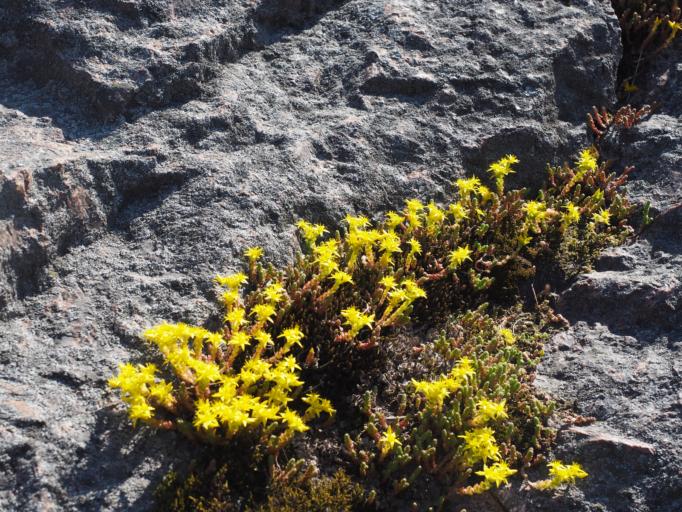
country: RU
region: Leningrad
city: Vyborg
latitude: 60.7088
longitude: 28.7362
